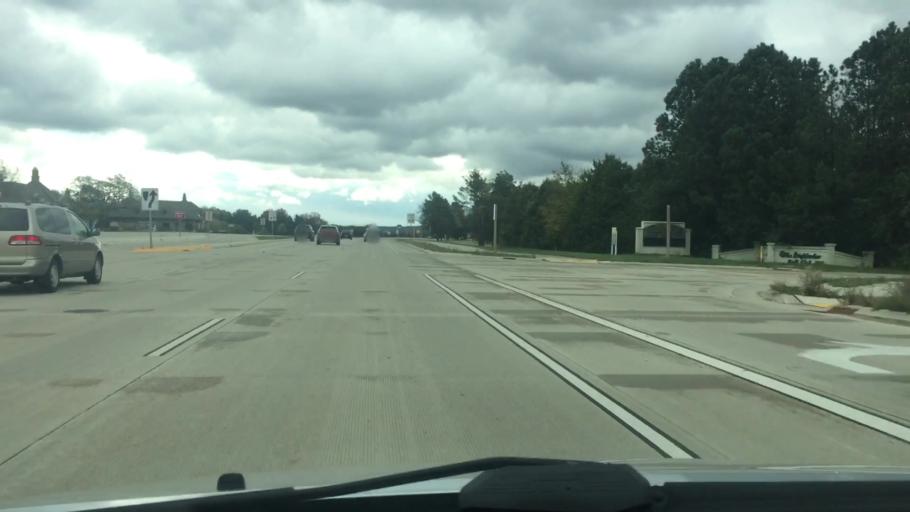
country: US
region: Wisconsin
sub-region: Waukesha County
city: Oconomowoc
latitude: 43.0909
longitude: -88.4752
